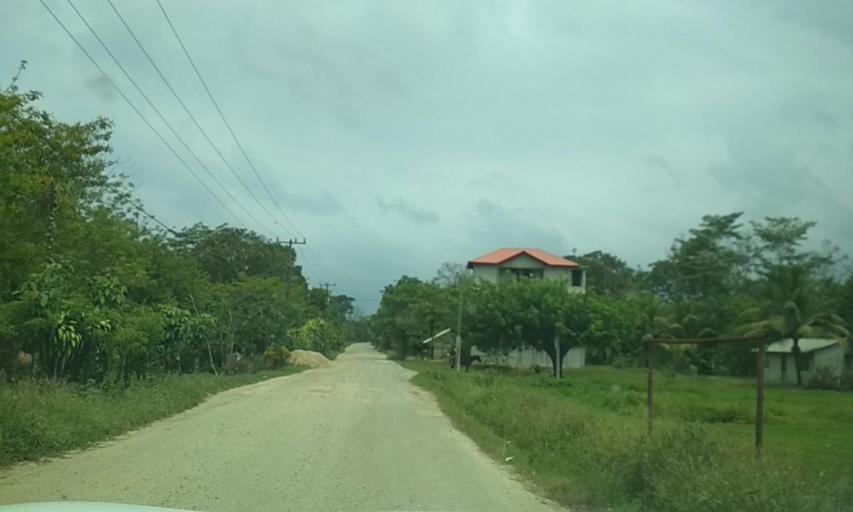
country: MX
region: Veracruz
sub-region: Uxpanapa
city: Poblado 10
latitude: 17.4980
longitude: -94.1447
